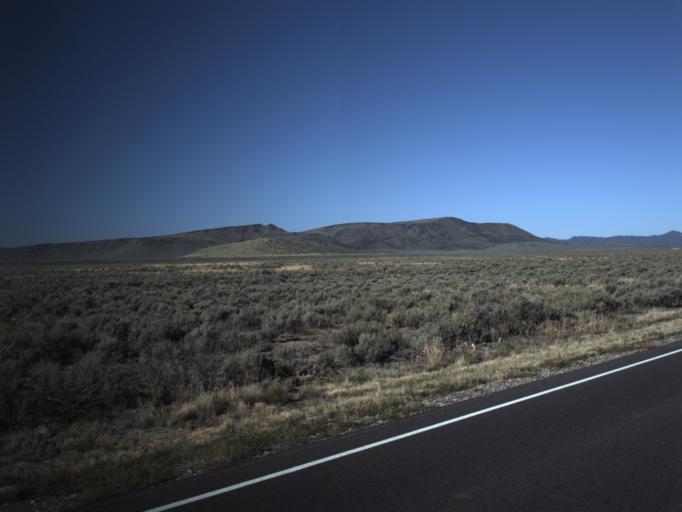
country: US
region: Utah
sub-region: Washington County
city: Enterprise
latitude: 37.7729
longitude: -113.8361
